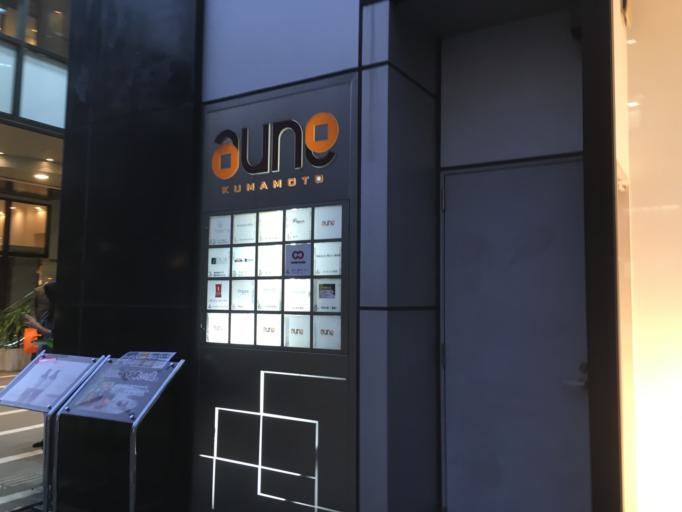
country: JP
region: Kumamoto
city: Kumamoto
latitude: 32.8033
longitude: 130.7100
